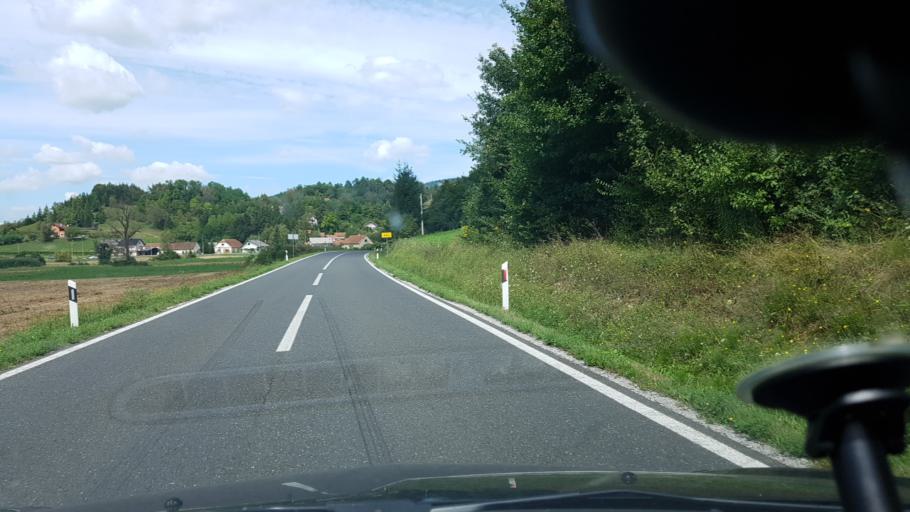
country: HR
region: Varazdinska
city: Lepoglava
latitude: 46.2263
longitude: 15.9932
